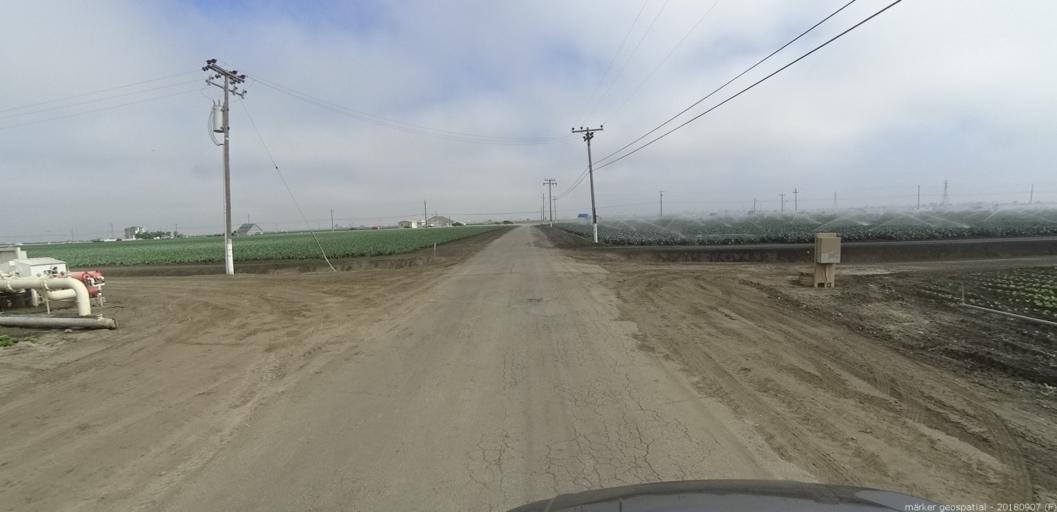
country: US
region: California
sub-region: Monterey County
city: Boronda
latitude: 36.6743
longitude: -121.7028
